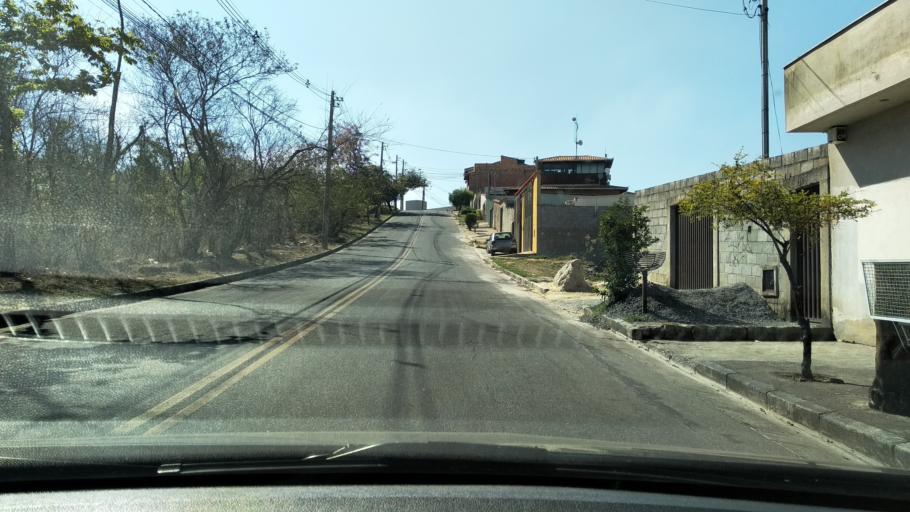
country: BR
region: Minas Gerais
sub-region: Belo Horizonte
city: Belo Horizonte
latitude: -19.8629
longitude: -43.8810
